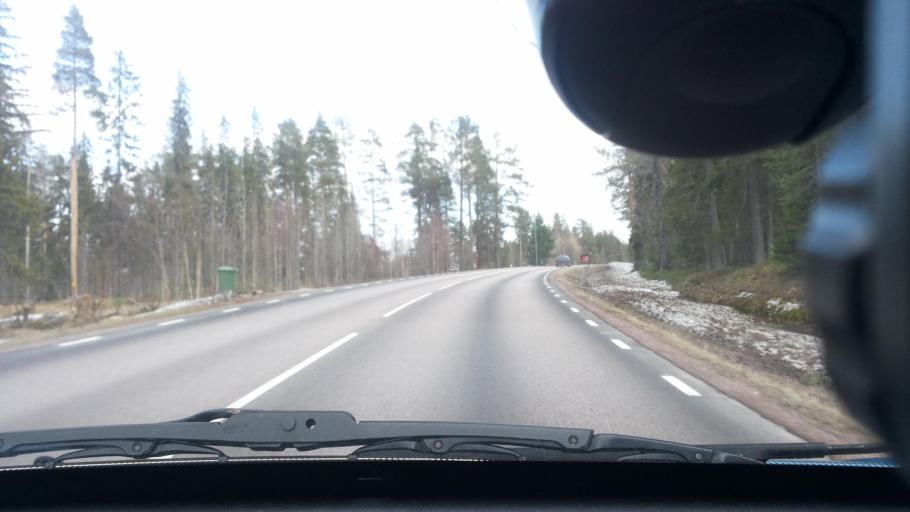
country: SE
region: Norrbotten
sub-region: Lulea Kommun
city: Gammelstad
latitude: 65.5998
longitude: 21.9876
